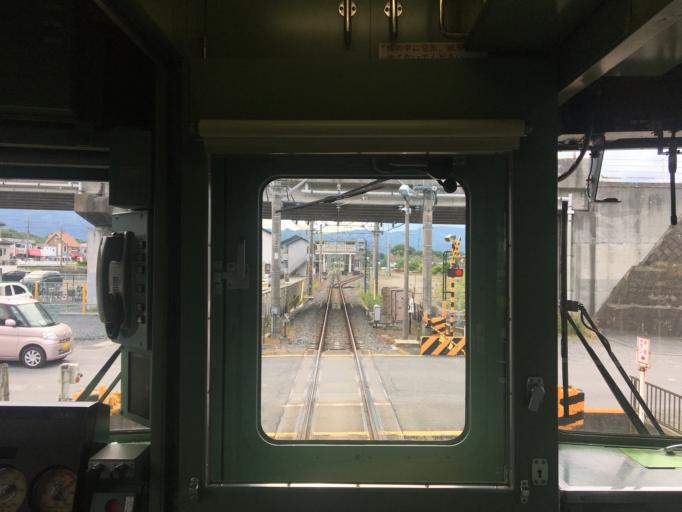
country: JP
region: Saitama
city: Yorii
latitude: 36.1141
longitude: 139.2111
